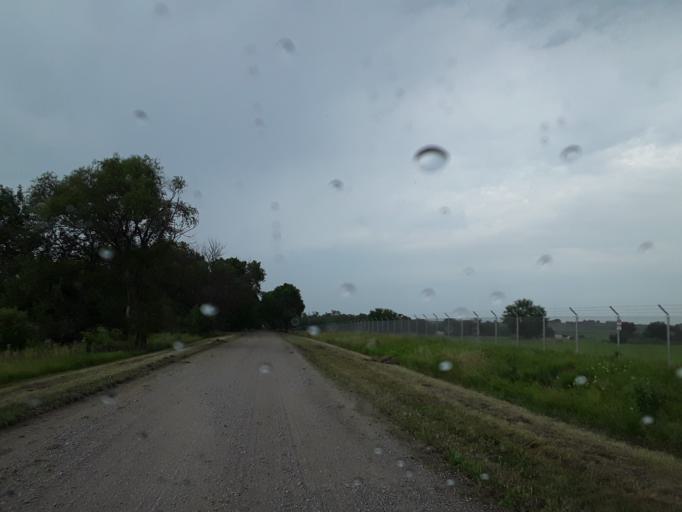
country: US
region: Nebraska
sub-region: Saunders County
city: Yutan
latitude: 41.1934
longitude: -96.4450
